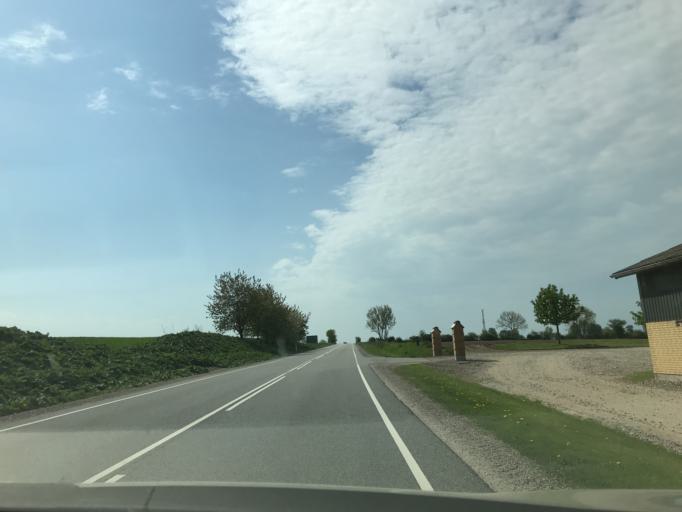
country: DK
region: South Denmark
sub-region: Middelfart Kommune
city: Ejby
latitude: 55.3834
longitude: 9.9180
